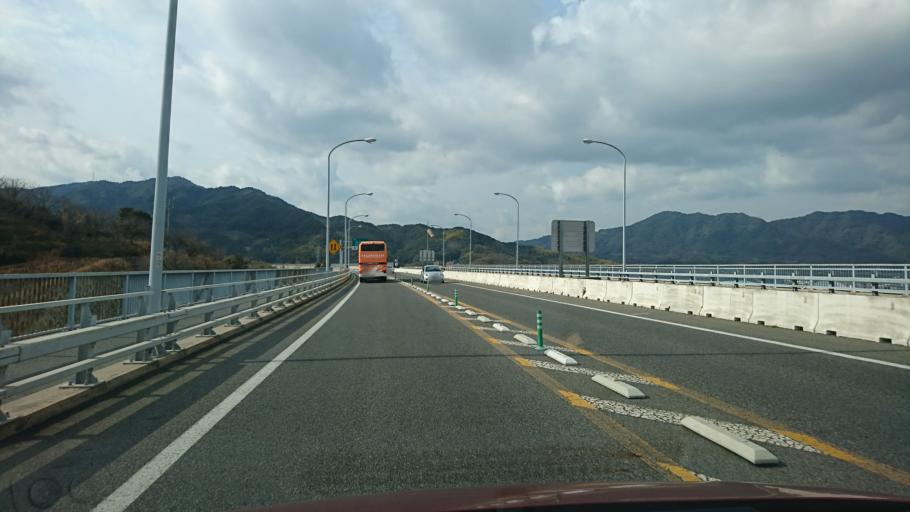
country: JP
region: Hiroshima
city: Innoshima
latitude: 34.2582
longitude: 133.0560
